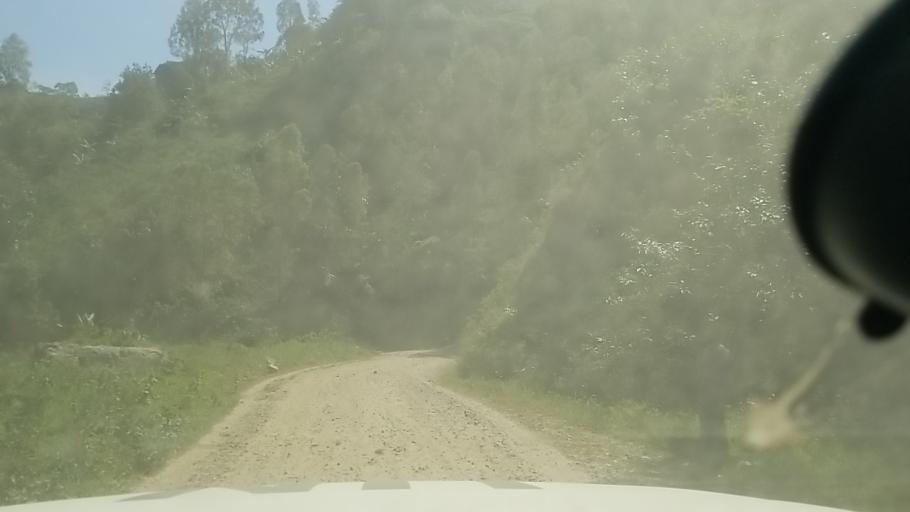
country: CD
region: Nord Kivu
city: Sake
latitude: -1.9695
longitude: 28.9144
